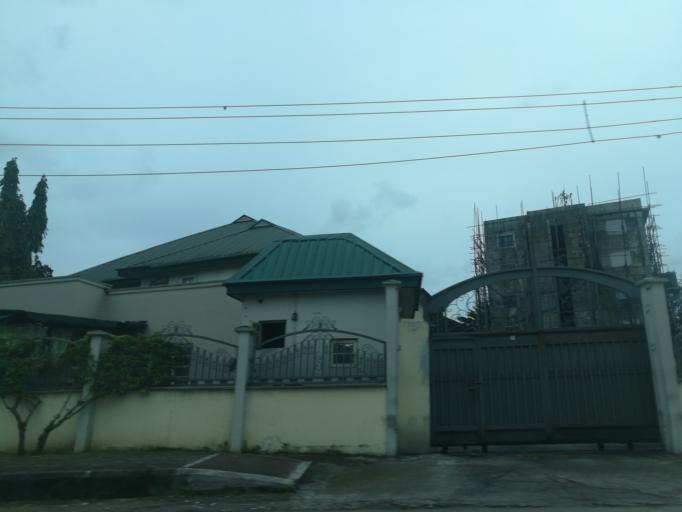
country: NG
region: Rivers
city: Port Harcourt
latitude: 4.8191
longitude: 6.9975
